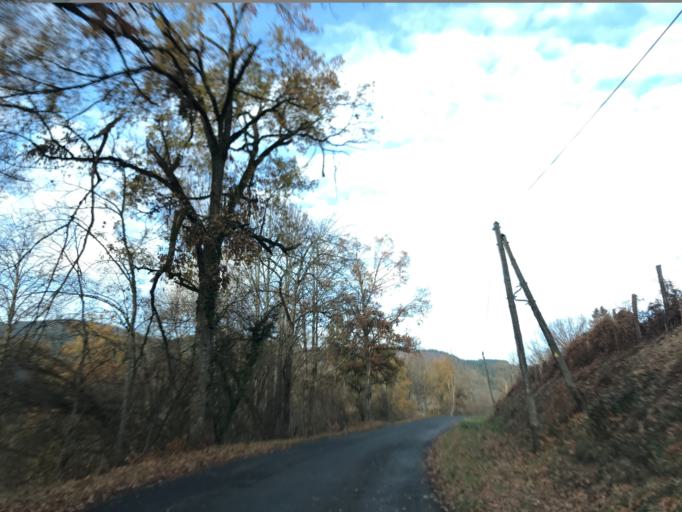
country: FR
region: Auvergne
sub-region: Departement du Puy-de-Dome
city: Celles-sur-Durolle
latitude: 45.7729
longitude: 3.6451
